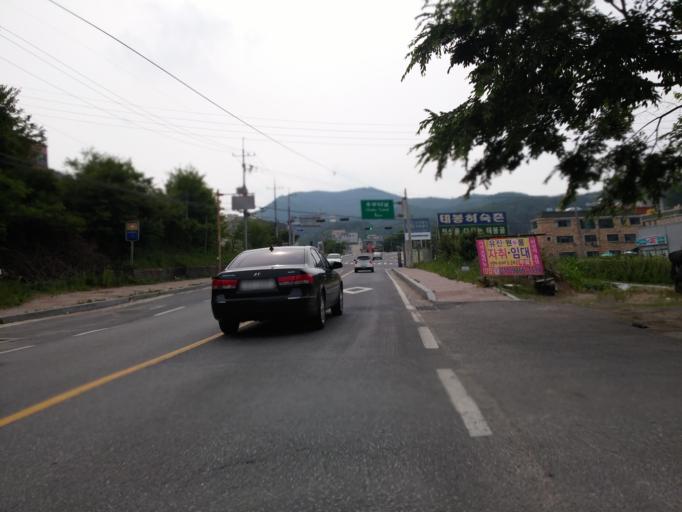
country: KR
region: Chungcheongnam-do
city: Kinzan
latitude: 36.1938
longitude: 127.4610
